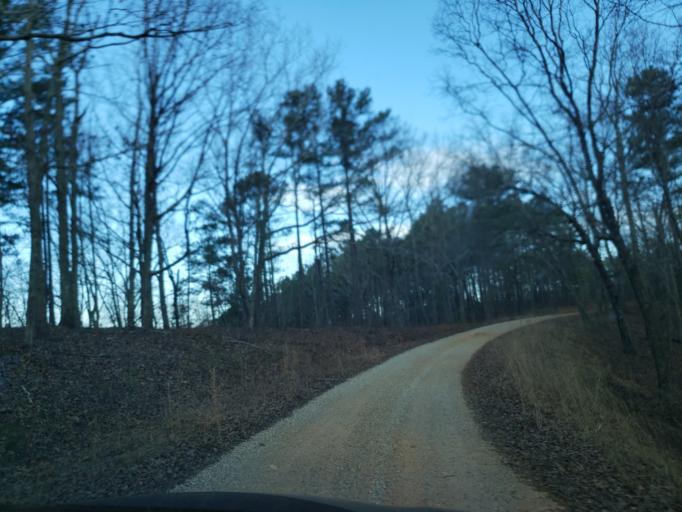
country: US
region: Alabama
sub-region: Cleburne County
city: Heflin
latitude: 33.6845
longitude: -85.6342
